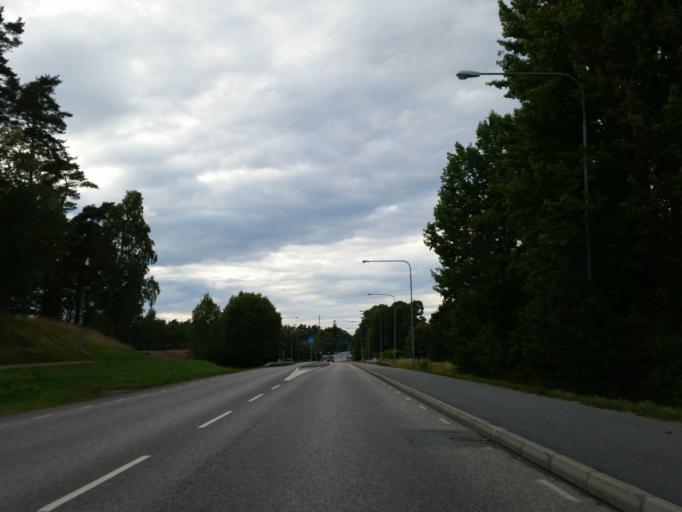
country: SE
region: Stockholm
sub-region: Upplands Vasby Kommun
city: Upplands Vaesby
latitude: 59.5381
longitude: 17.9167
